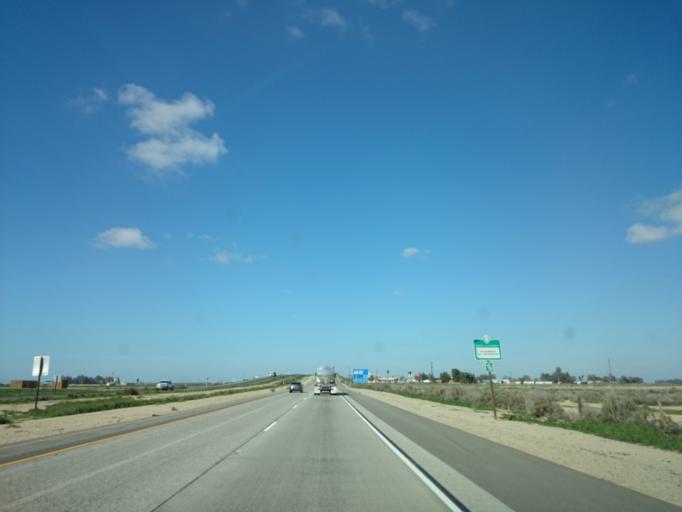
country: US
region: California
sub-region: Kern County
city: Buttonwillow
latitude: 35.3941
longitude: -119.3905
